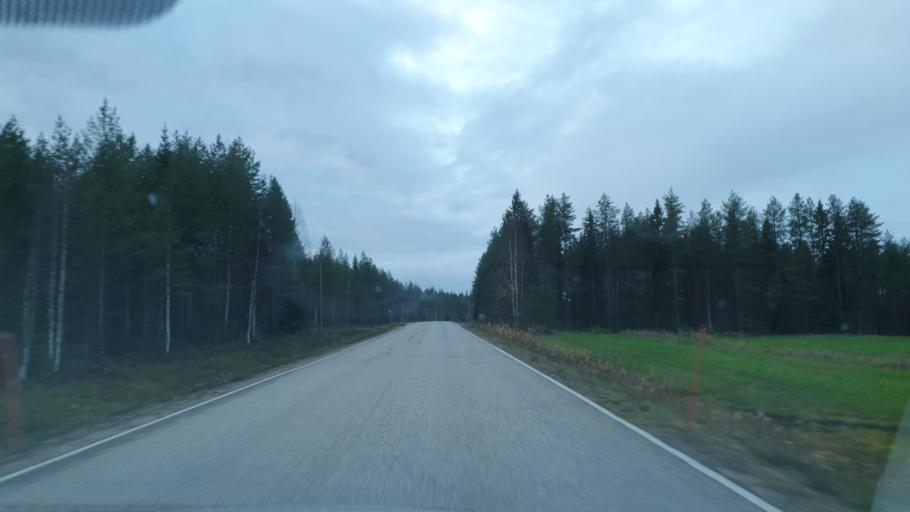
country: FI
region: Kainuu
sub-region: Kajaani
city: Ristijaervi
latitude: 64.4215
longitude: 28.4061
